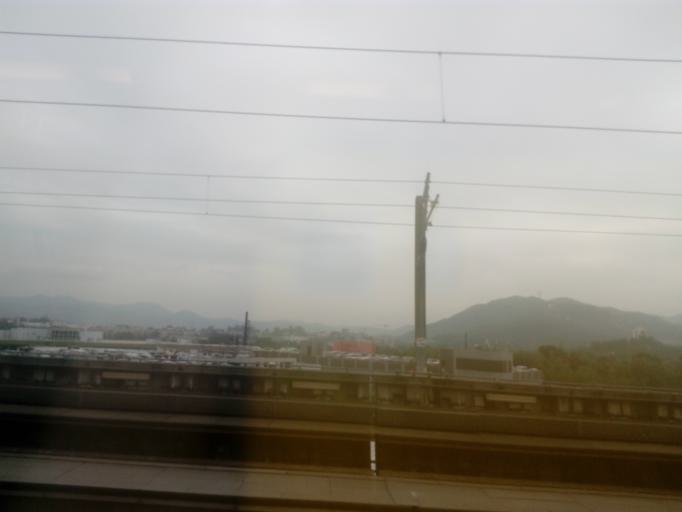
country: HK
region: Yuen Long
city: Yuen Long Kau Hui
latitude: 22.4451
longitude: 114.0012
